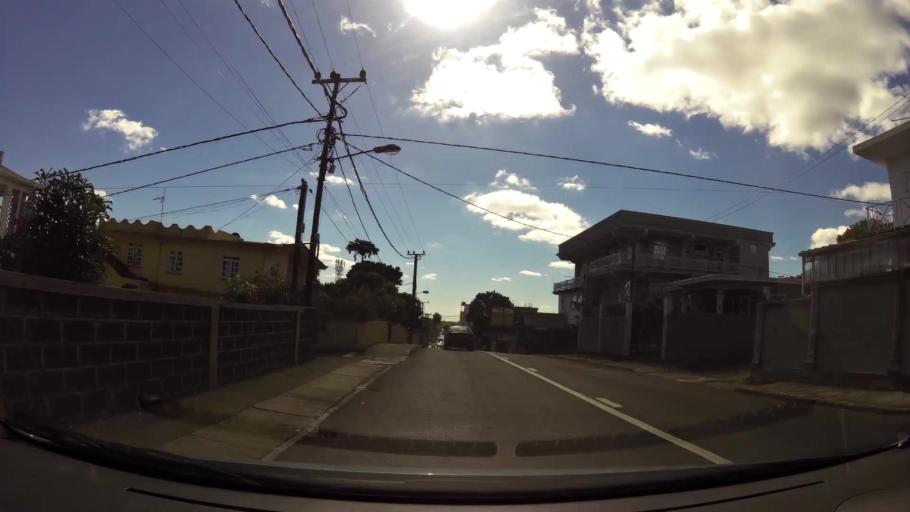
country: MU
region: Plaines Wilhems
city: Quatre Bornes
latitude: -20.2804
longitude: 57.4783
